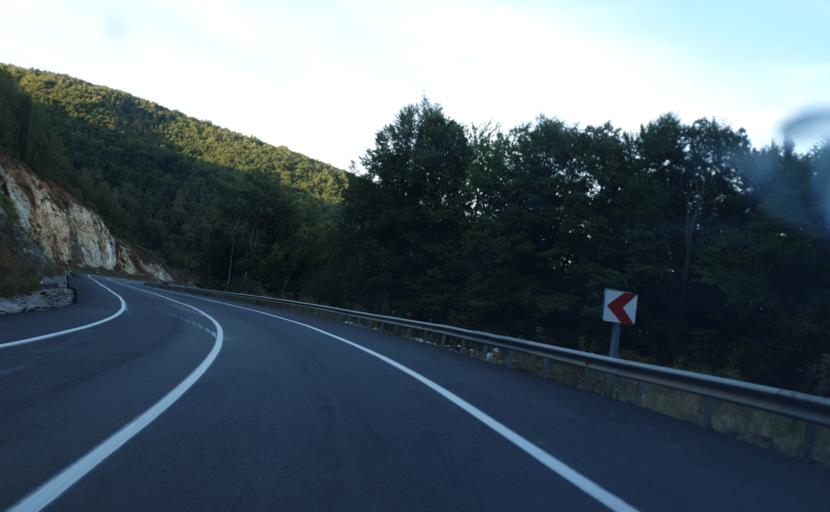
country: TR
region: Kirklareli
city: Sergen
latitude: 41.8080
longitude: 27.7389
